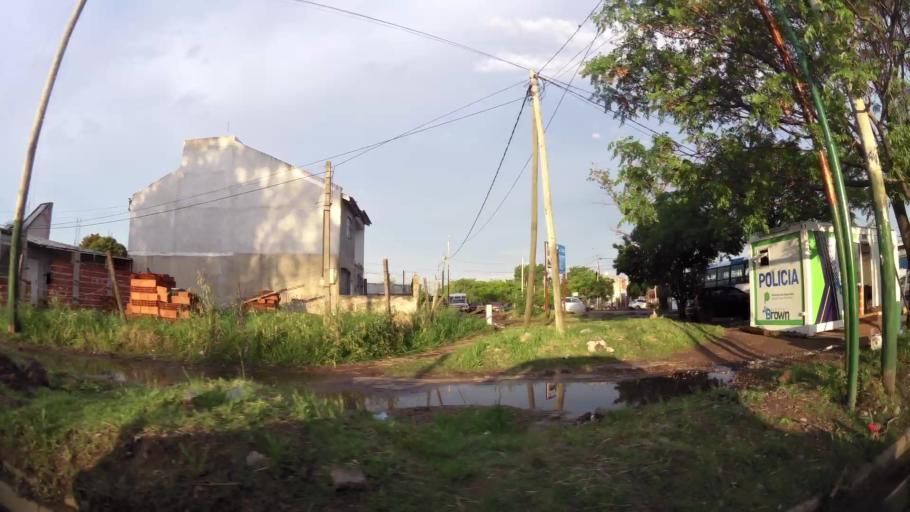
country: AR
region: Buenos Aires
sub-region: Partido de Almirante Brown
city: Adrogue
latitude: -34.7660
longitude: -58.3415
